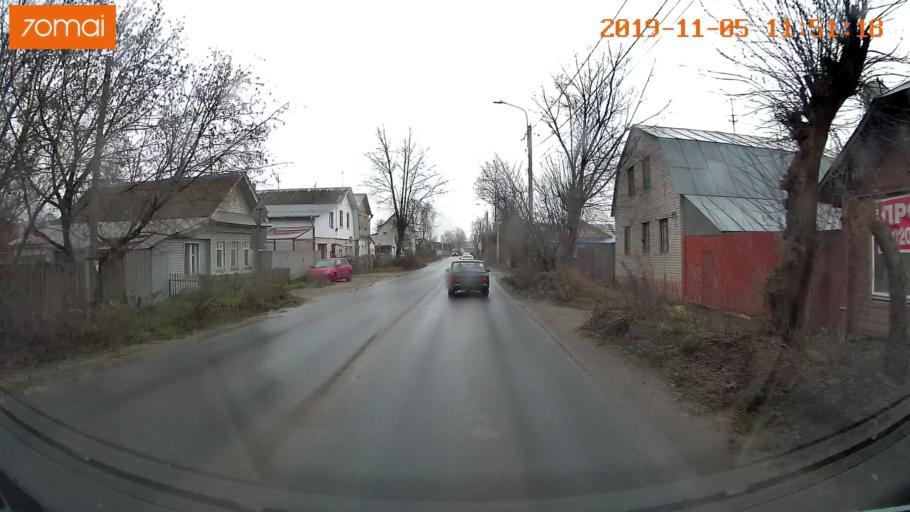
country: RU
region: Ivanovo
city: Bogorodskoye
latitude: 57.0064
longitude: 41.0264
